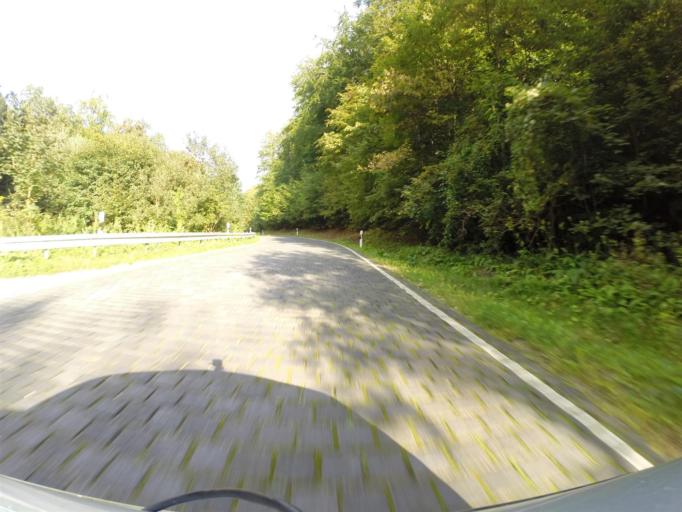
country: DE
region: Thuringia
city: Lehesten
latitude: 50.9559
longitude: 11.5818
